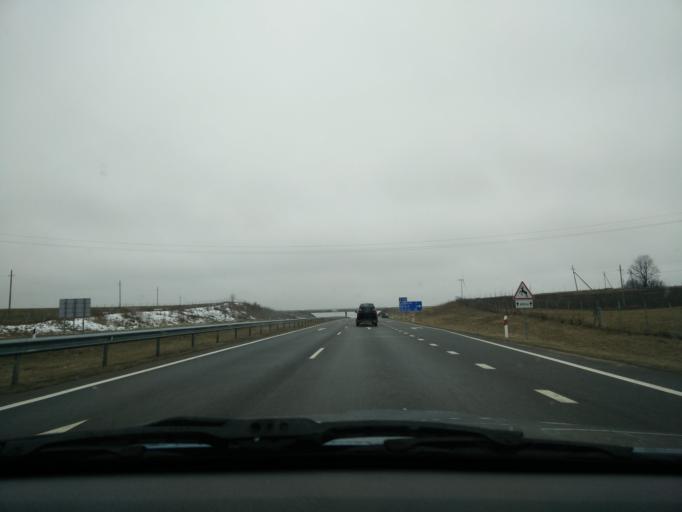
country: LT
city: Silale
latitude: 55.5588
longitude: 22.2269
